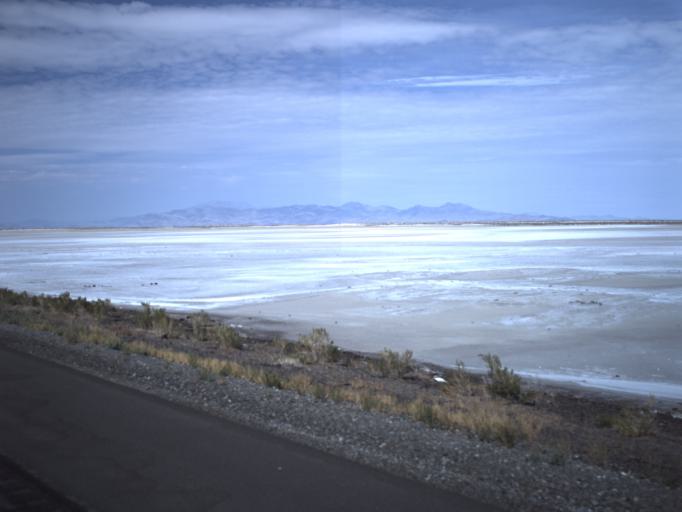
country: US
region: Utah
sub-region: Tooele County
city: Wendover
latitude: 40.7304
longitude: -113.4378
